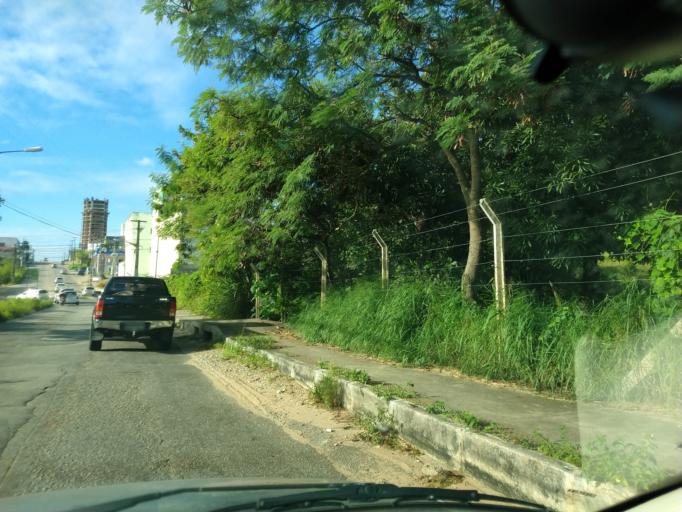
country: BR
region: Rio Grande do Norte
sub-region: Natal
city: Natal
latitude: -5.8330
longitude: -35.2234
